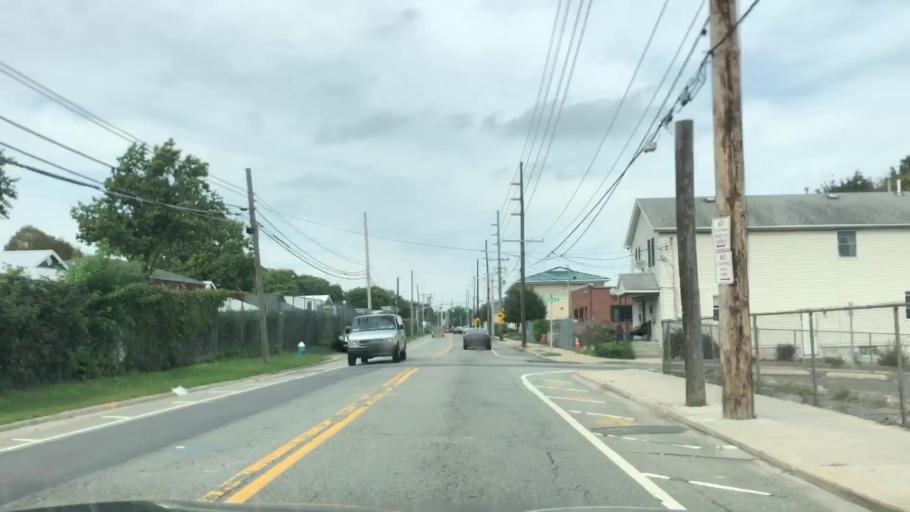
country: US
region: New York
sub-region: Nassau County
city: South Floral Park
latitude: 40.7114
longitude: -73.7087
